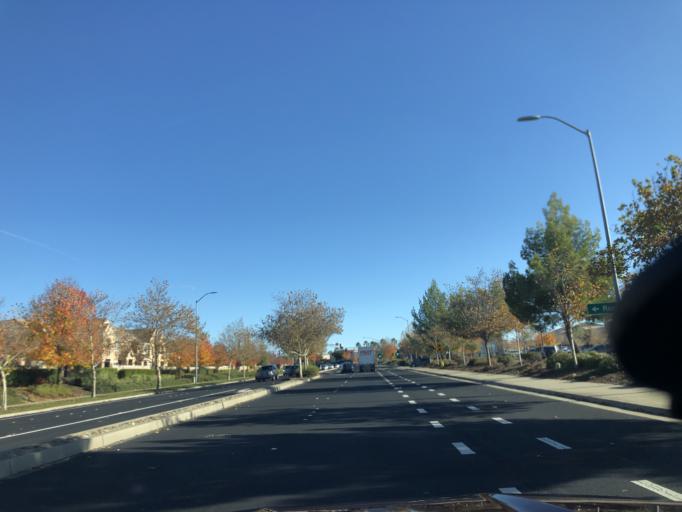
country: US
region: California
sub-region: Placer County
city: Roseville
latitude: 38.7915
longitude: -121.2888
